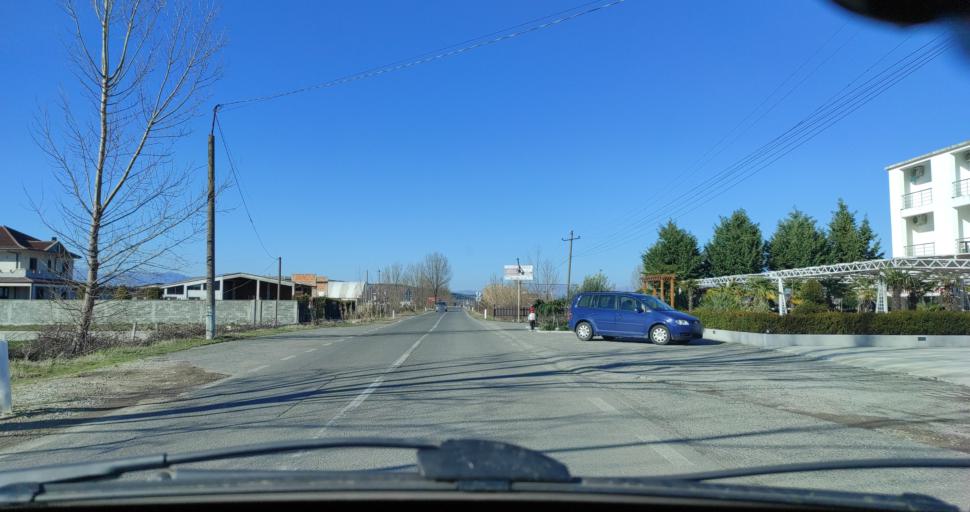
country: AL
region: Shkoder
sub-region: Rrethi i Shkodres
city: Velipoje
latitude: 41.8797
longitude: 19.4038
